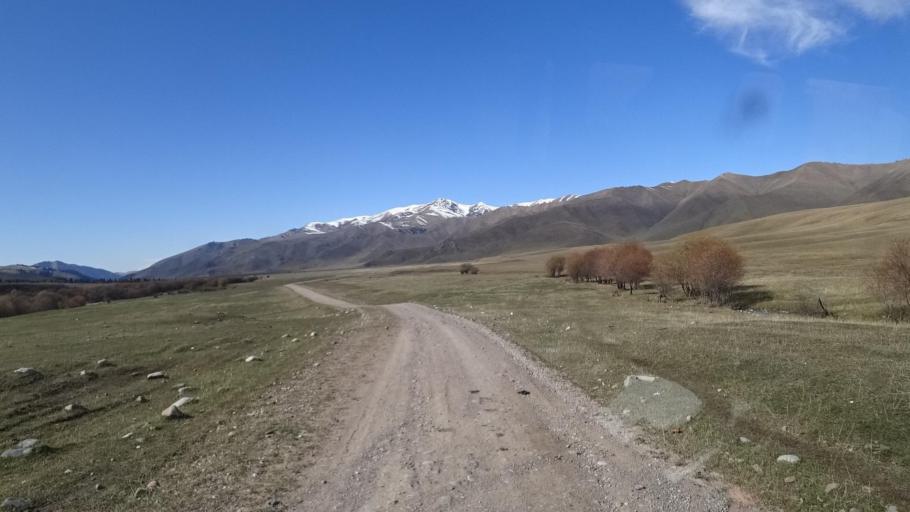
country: KZ
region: Almaty Oblysy
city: Kegen
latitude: 42.7367
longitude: 79.0147
